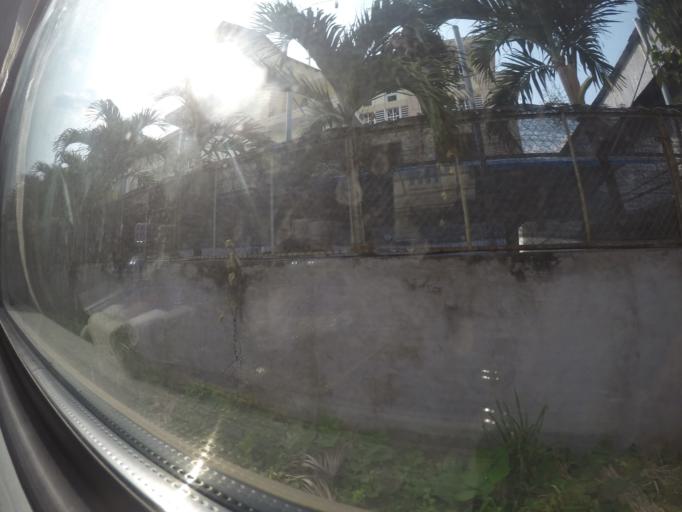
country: VN
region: Dong Nai
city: Bien Hoa
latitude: 10.9610
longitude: 106.8370
